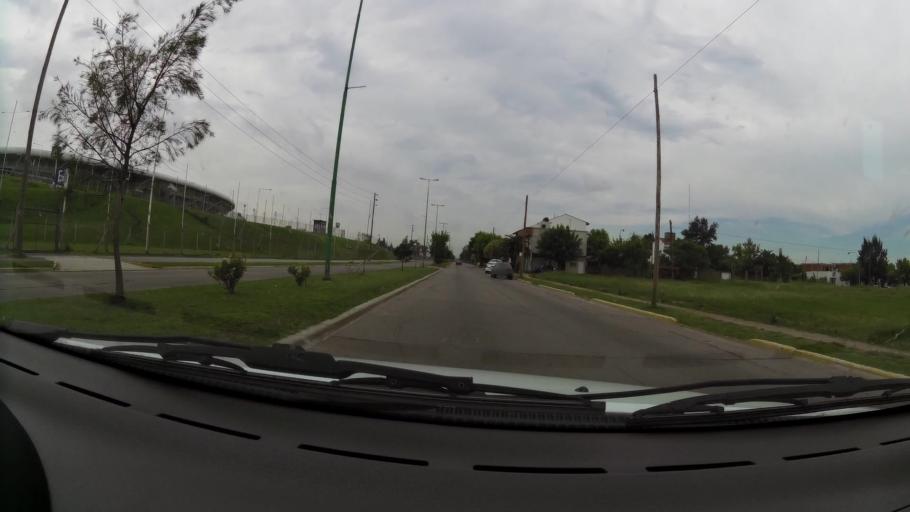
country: AR
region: Buenos Aires
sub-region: Partido de La Plata
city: La Plata
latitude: -34.9146
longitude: -57.9913
